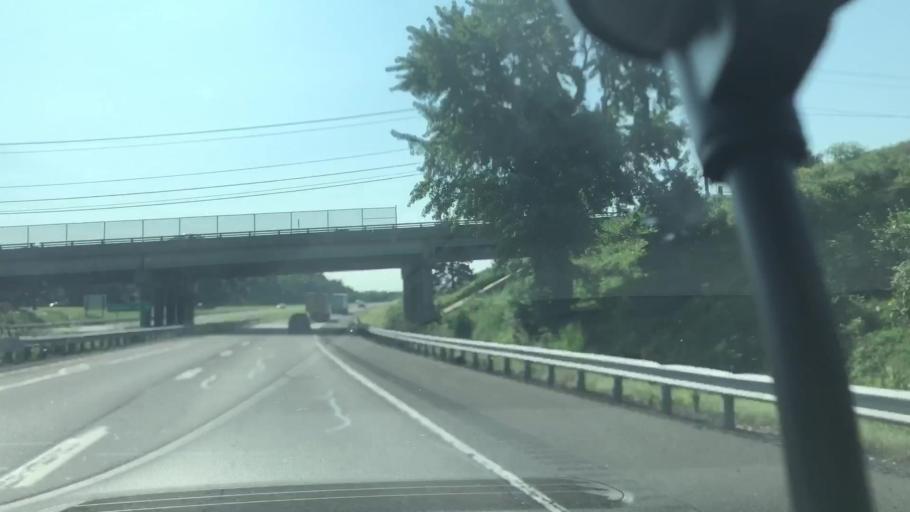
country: US
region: Pennsylvania
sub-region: Montgomery County
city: Royersford
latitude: 40.1957
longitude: -75.5258
